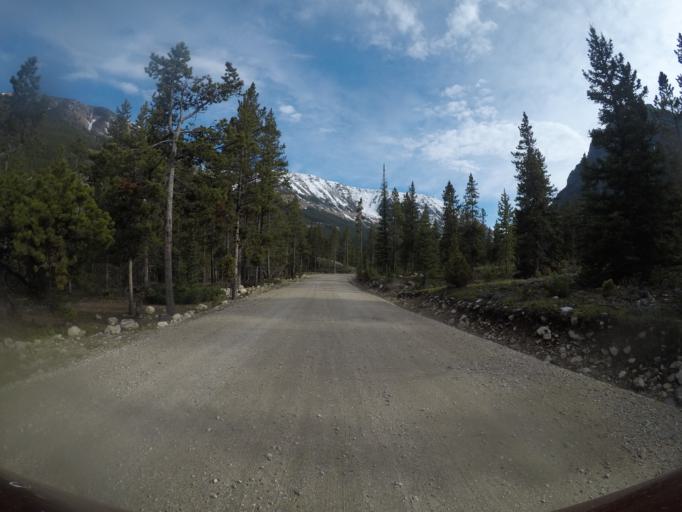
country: US
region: Montana
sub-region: Carbon County
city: Red Lodge
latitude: 45.0445
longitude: -109.4260
